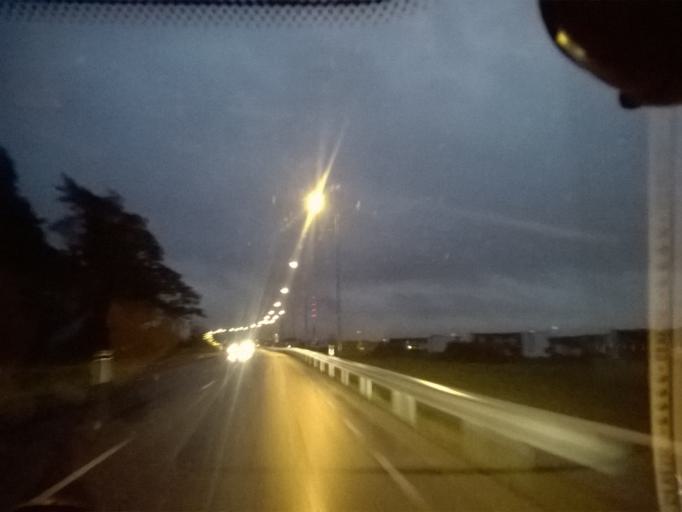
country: EE
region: Harju
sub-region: Viimsi vald
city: Viimsi
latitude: 59.5030
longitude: 24.8674
